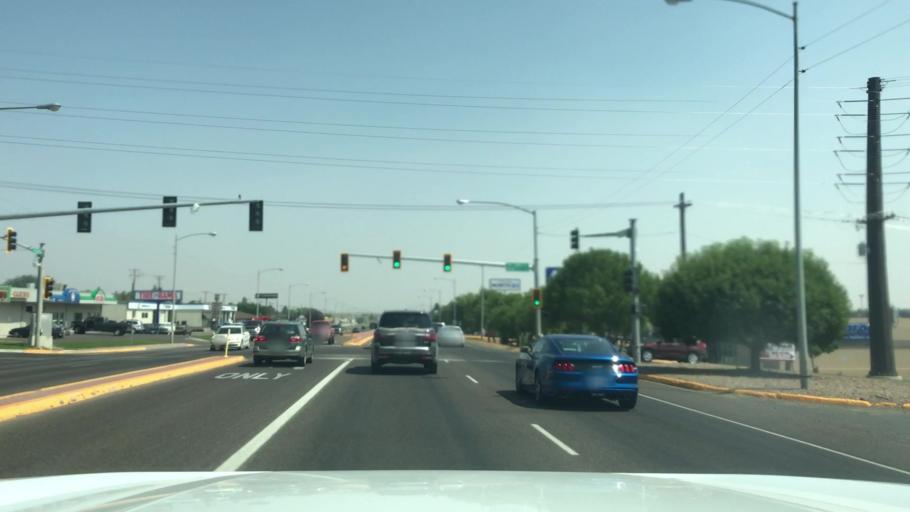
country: US
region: Montana
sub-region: Cascade County
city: Malmstrom Air Force Base
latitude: 47.4939
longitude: -111.2337
